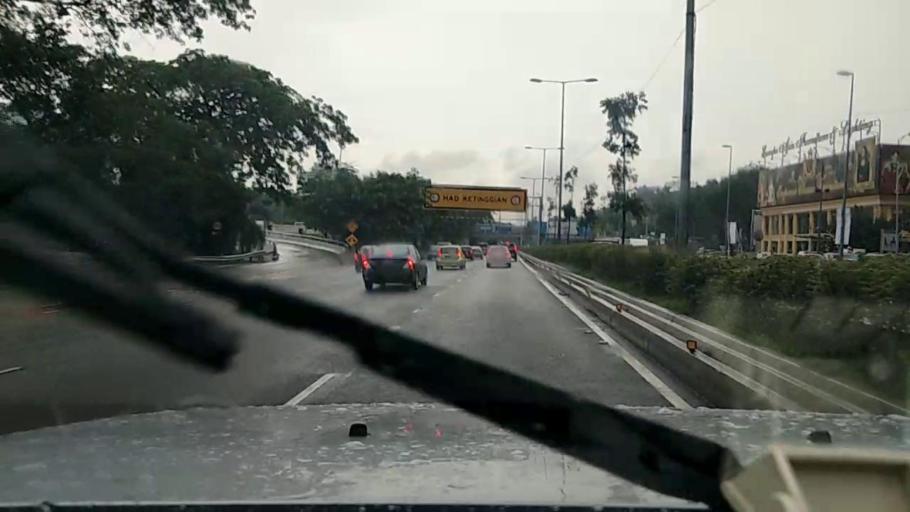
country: MY
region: Kuala Lumpur
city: Kuala Lumpur
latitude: 3.1227
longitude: 101.6809
